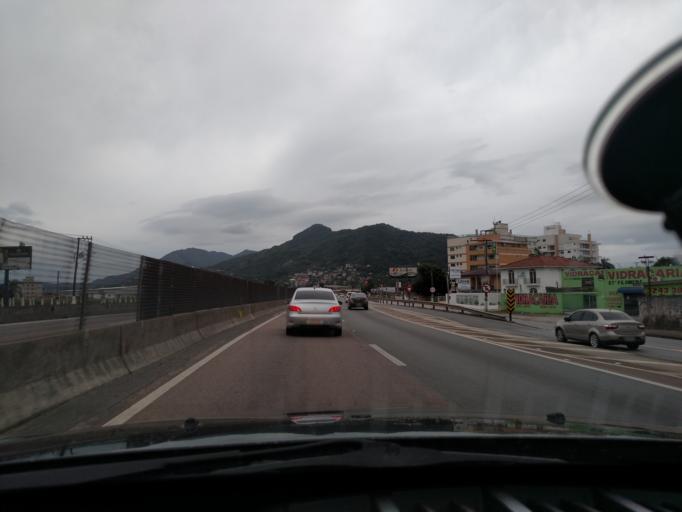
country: BR
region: Santa Catarina
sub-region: Biguacu
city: Biguacu
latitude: -27.4968
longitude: -48.6570
